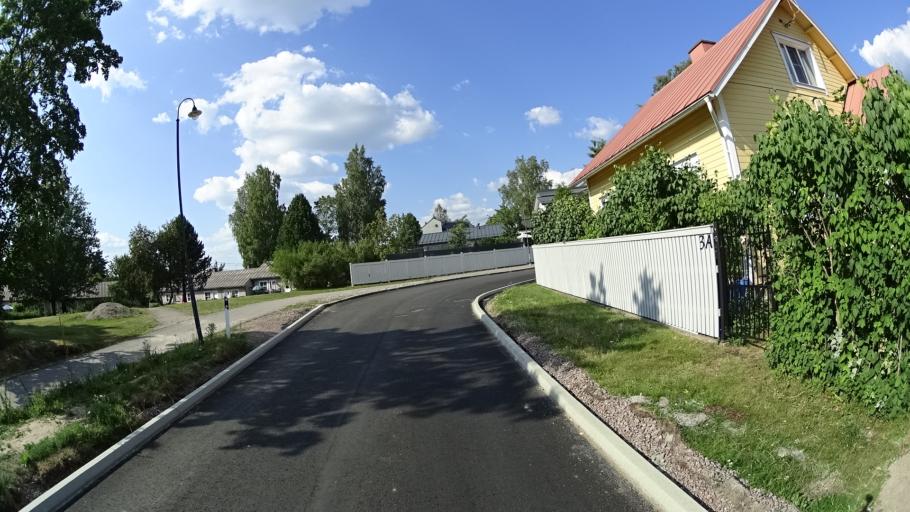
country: FI
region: Uusimaa
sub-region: Porvoo
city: Porvoo
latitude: 60.4003
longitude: 25.6642
